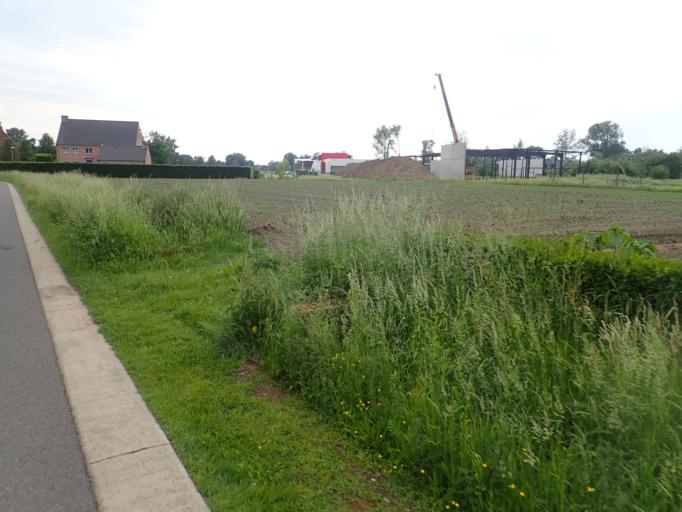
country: BE
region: Flanders
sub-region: Provincie Antwerpen
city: Vosselaar
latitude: 51.2505
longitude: 4.8981
